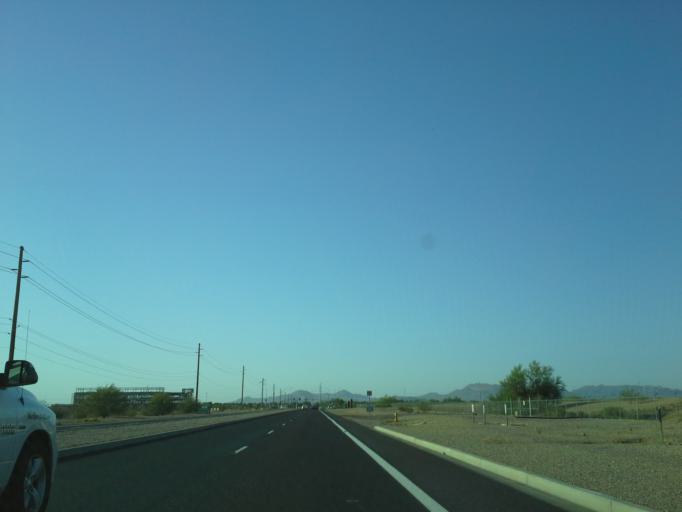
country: US
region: Arizona
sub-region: Maricopa County
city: Queen Creek
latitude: 33.3457
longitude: -111.6356
